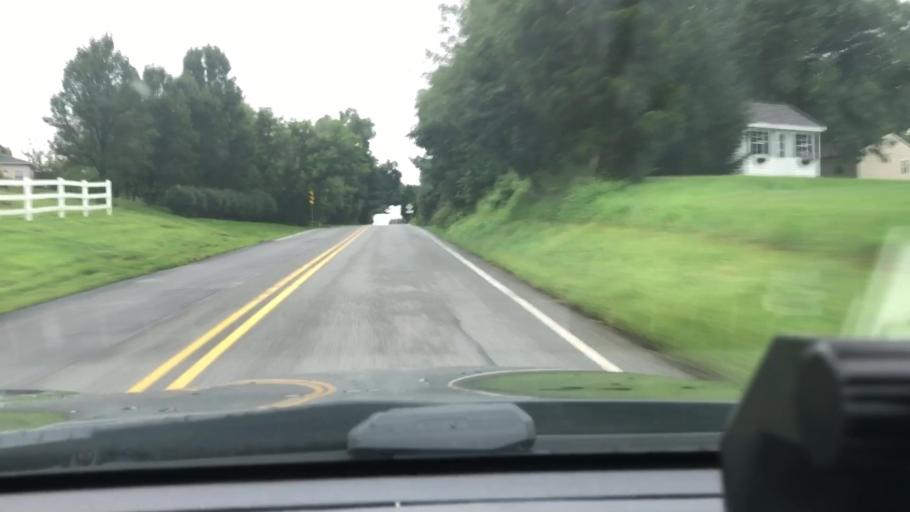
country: US
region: Pennsylvania
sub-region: Montgomery County
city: Gilbertsville
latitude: 40.3055
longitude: -75.6168
